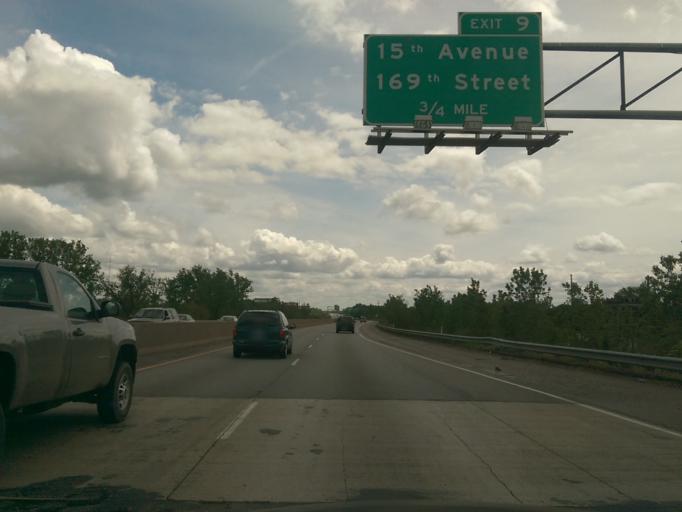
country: US
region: Indiana
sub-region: Lake County
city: East Chicago
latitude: 41.5995
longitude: -87.4327
